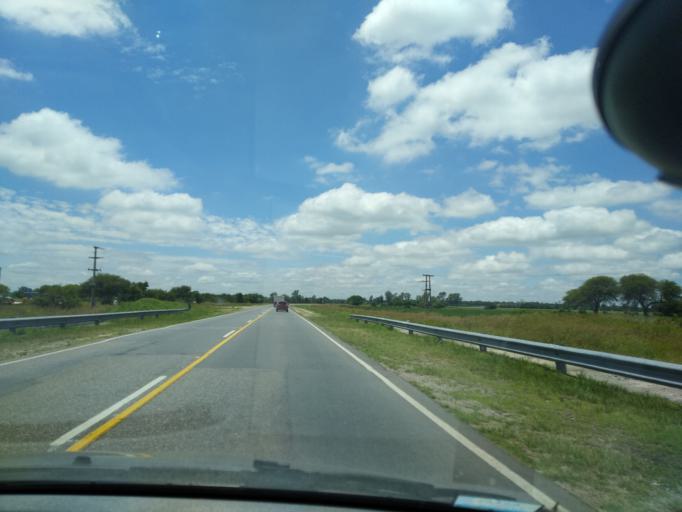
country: AR
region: Cordoba
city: Alta Gracia
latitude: -31.6550
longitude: -64.3515
